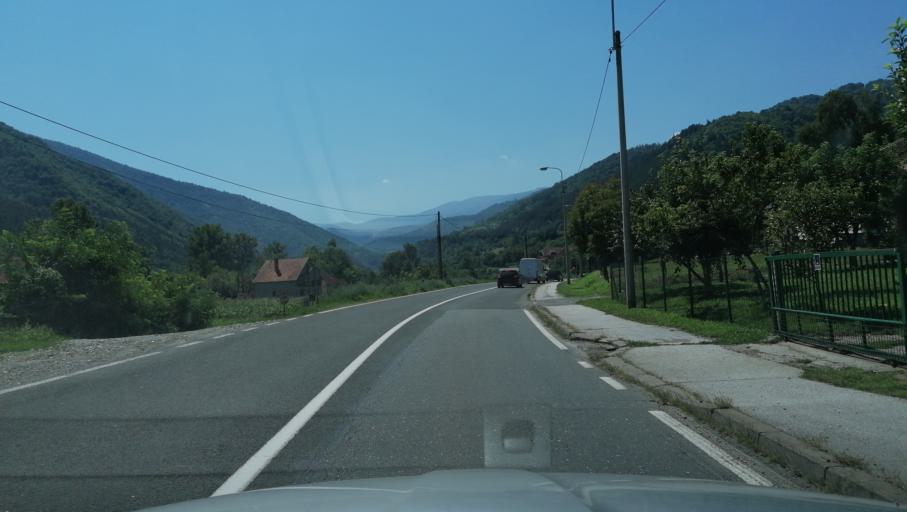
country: RS
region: Central Serbia
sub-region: Raski Okrug
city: Kraljevo
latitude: 43.6516
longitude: 20.5556
